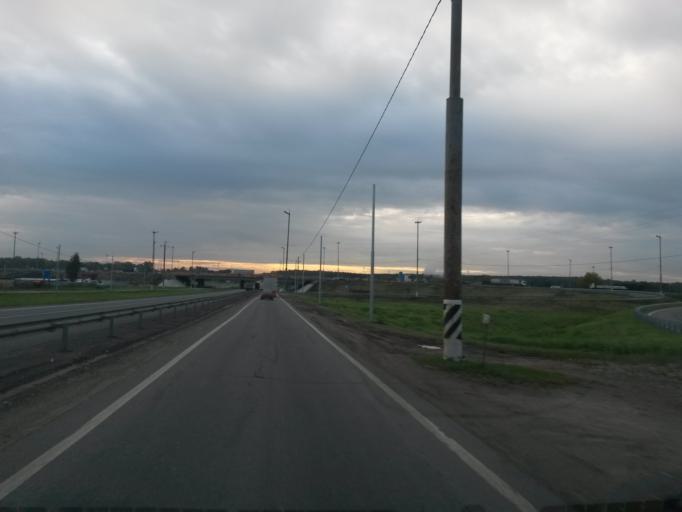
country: RU
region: Moskovskaya
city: L'vovskiy
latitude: 55.3319
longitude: 37.5612
